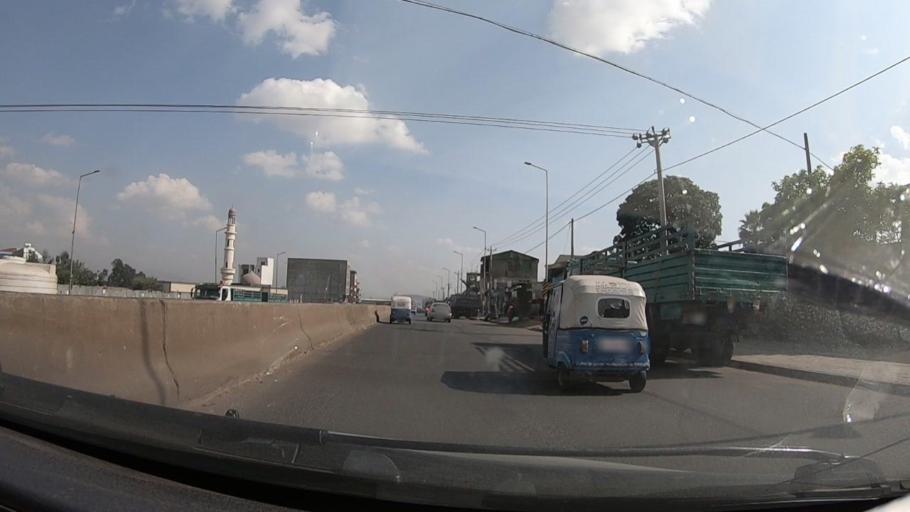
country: ET
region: Adis Abeba
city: Addis Ababa
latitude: 8.9894
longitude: 38.6915
